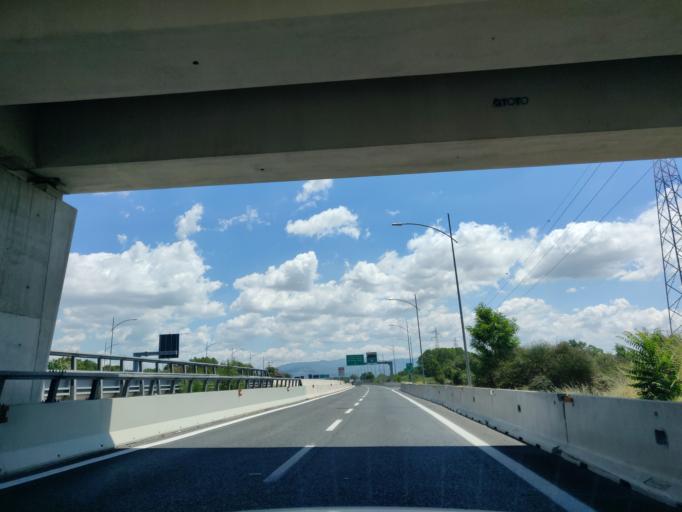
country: IT
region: Latium
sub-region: Citta metropolitana di Roma Capitale
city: Setteville
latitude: 41.9230
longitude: 12.6297
